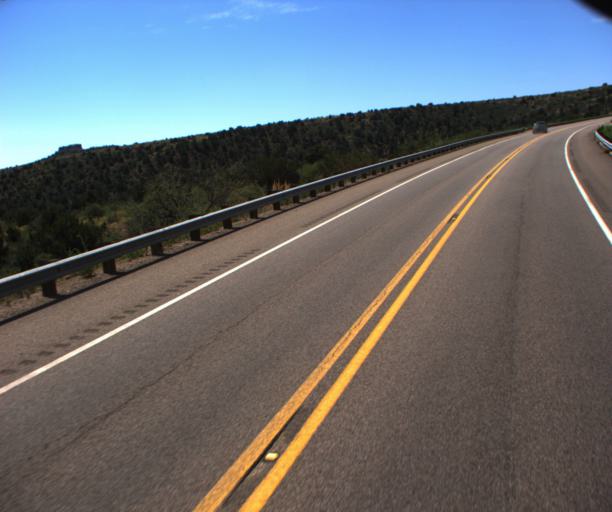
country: US
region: Arizona
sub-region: Gila County
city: Globe
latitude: 33.5556
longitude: -110.6783
